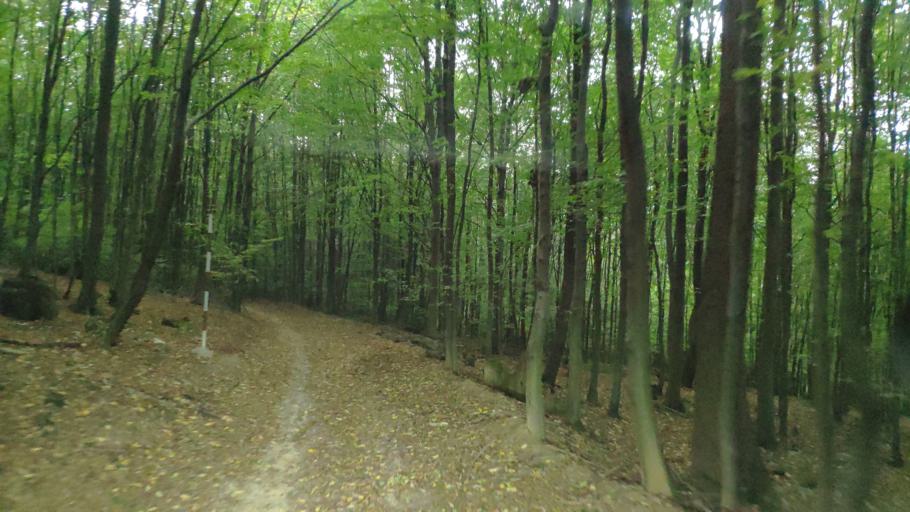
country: SK
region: Kosicky
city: Kosice
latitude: 48.7003
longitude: 21.1974
